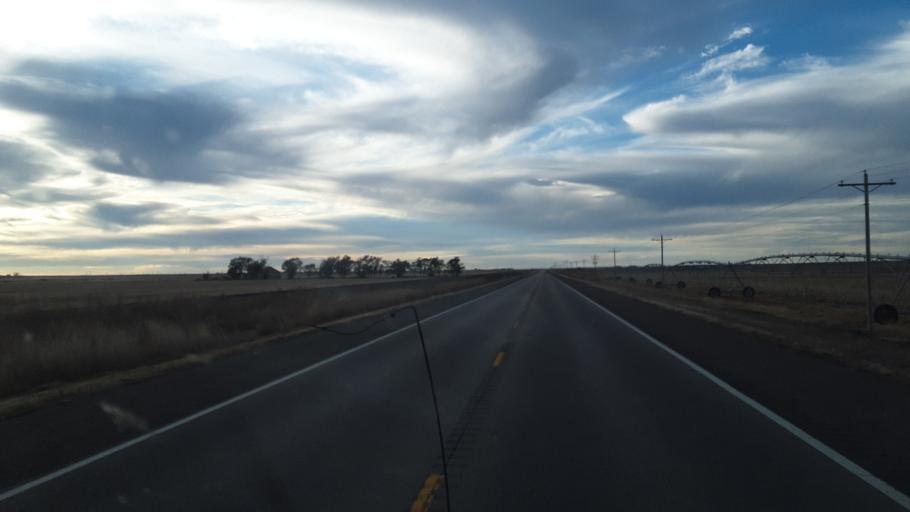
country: US
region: Kansas
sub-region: Hamilton County
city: Syracuse
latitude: 38.0033
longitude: -101.8415
